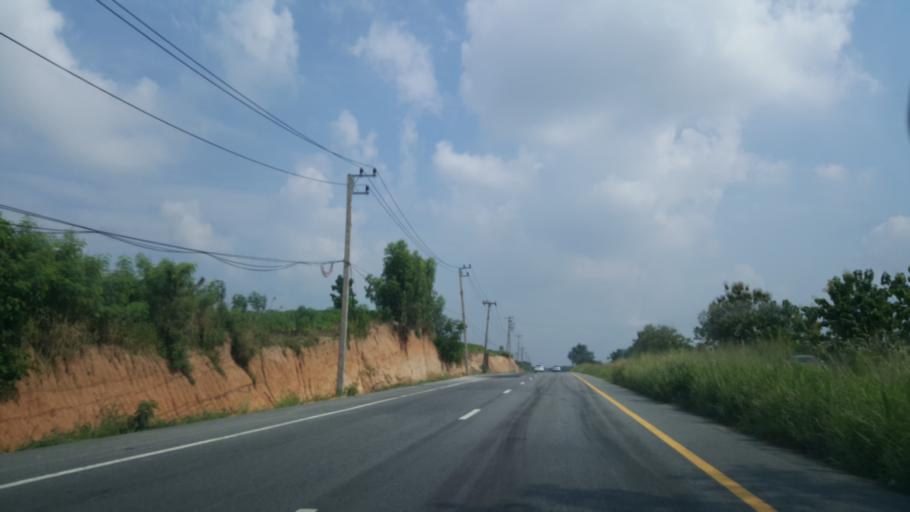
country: TH
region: Rayong
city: Ban Chang
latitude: 12.8500
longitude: 101.0168
